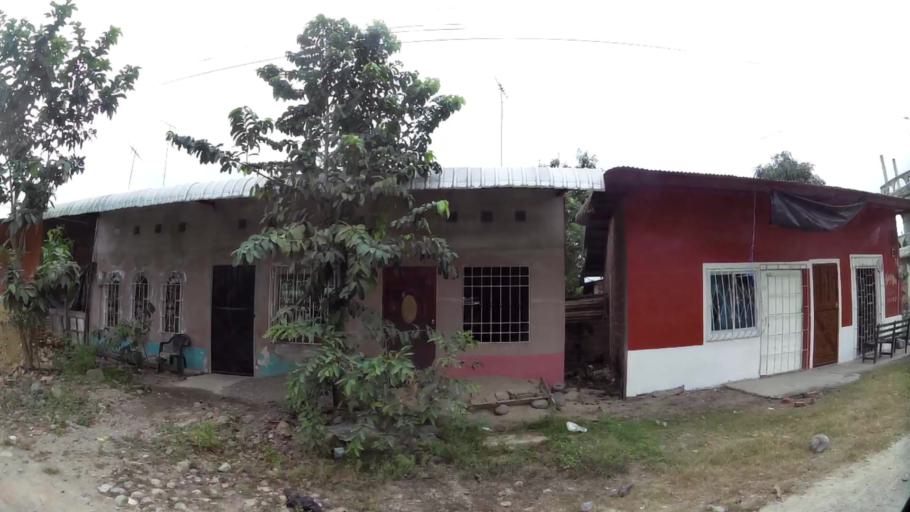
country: EC
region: Guayas
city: Naranjal
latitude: -2.6761
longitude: -79.6270
